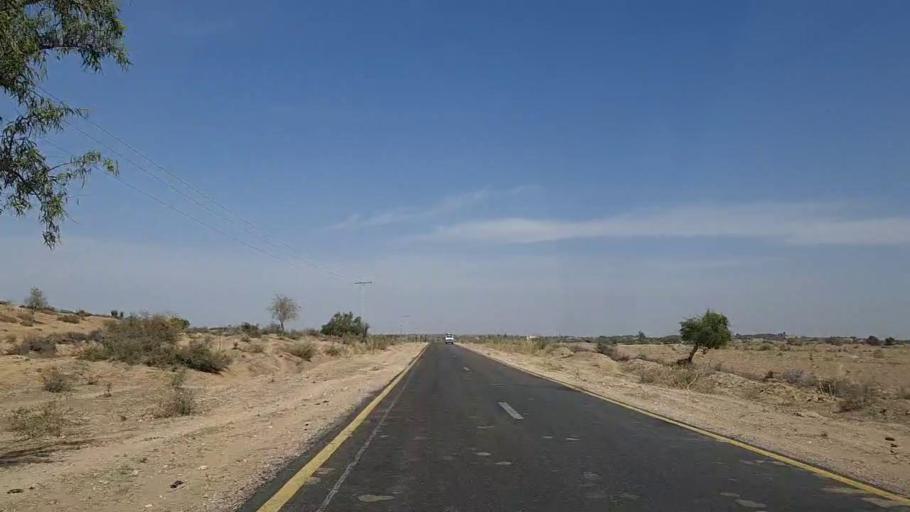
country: PK
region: Sindh
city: Mithi
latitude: 24.9597
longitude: 69.9079
